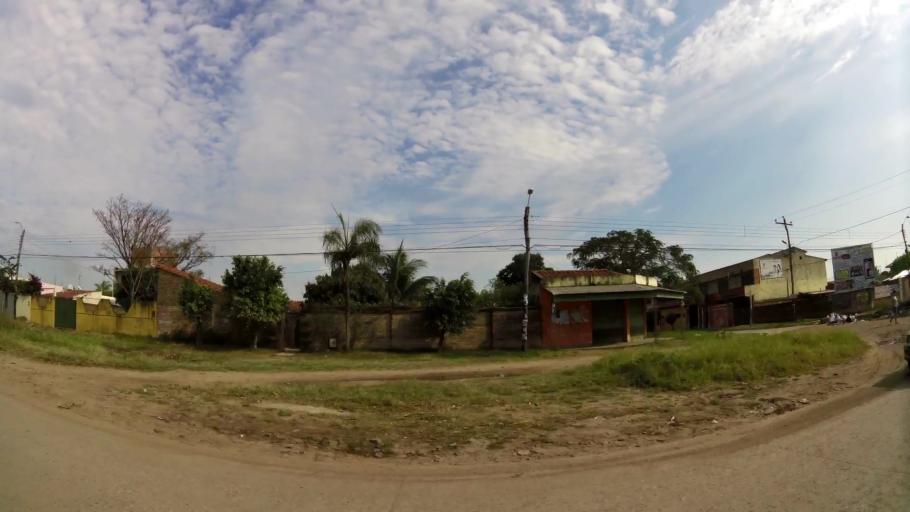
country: BO
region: Santa Cruz
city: Santa Cruz de la Sierra
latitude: -17.7316
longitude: -63.1416
